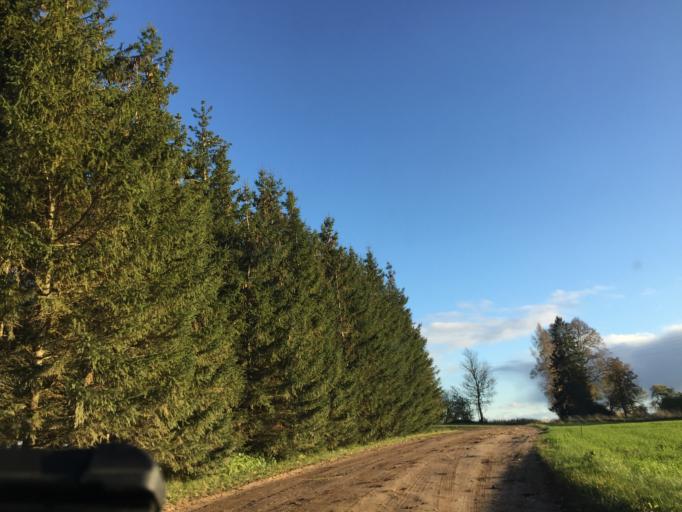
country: LV
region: Saldus Rajons
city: Saldus
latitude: 56.8127
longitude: 22.3834
